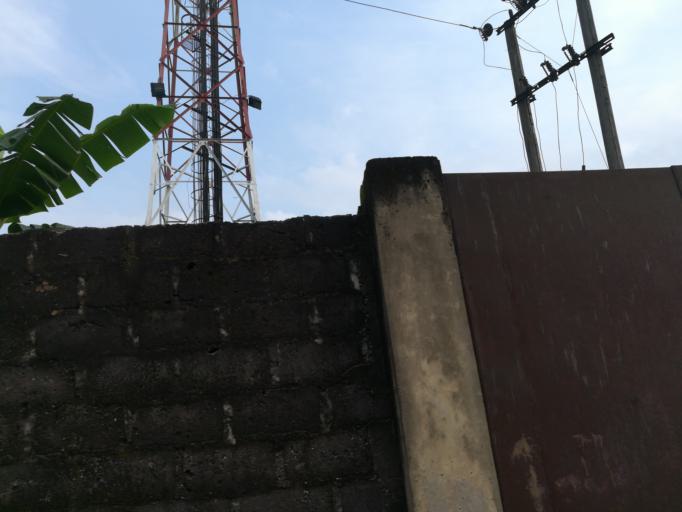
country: NG
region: Rivers
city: Port Harcourt
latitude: 4.8437
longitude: 7.0546
